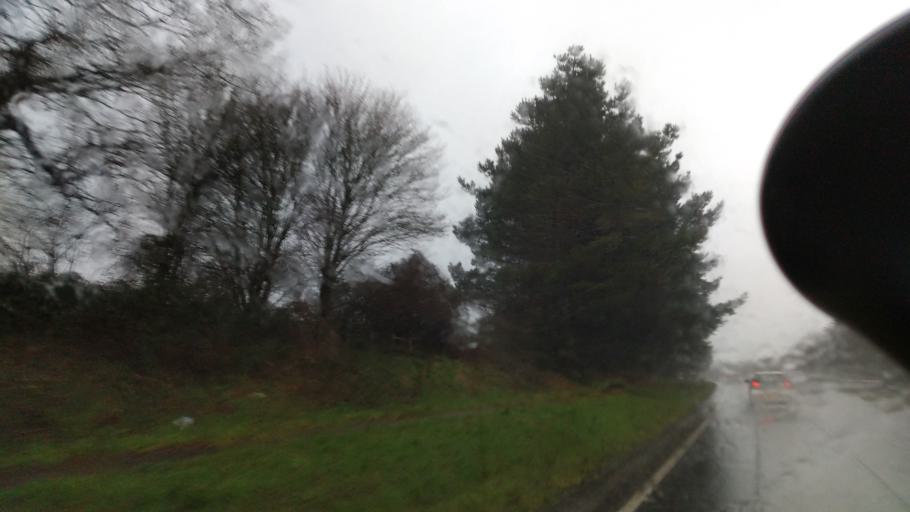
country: GB
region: England
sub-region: West Sussex
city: Fontwell
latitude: 50.8566
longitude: -0.6571
